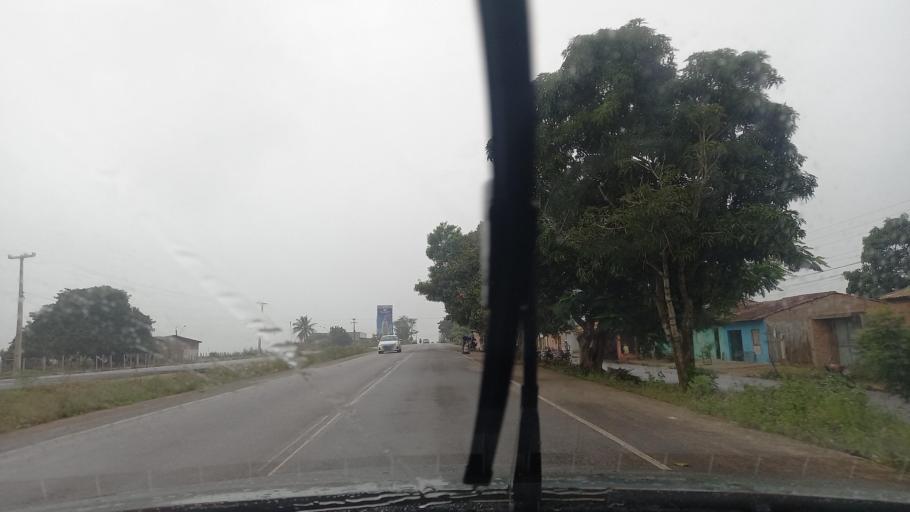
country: BR
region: Alagoas
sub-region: Lagoa Da Canoa
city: Lagoa da Canoa
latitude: -9.7005
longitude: -36.7986
